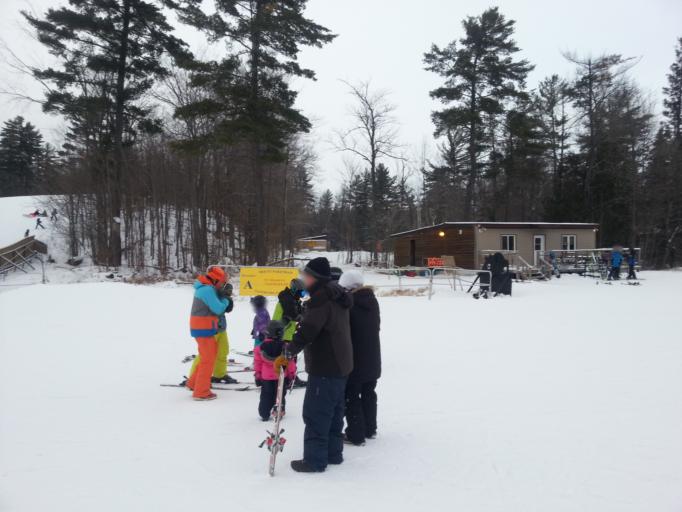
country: CA
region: Ontario
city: Arnprior
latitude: 45.3231
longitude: -76.3314
